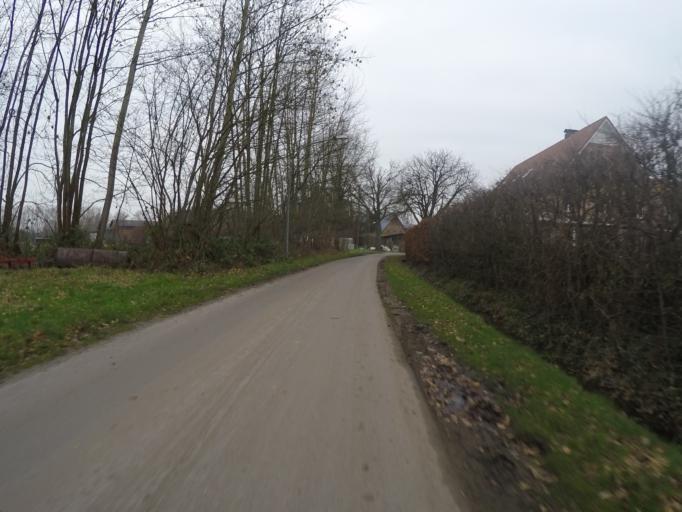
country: DE
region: Schleswig-Holstein
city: Borstel-Hohenraden
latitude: 53.6836
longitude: 9.8165
